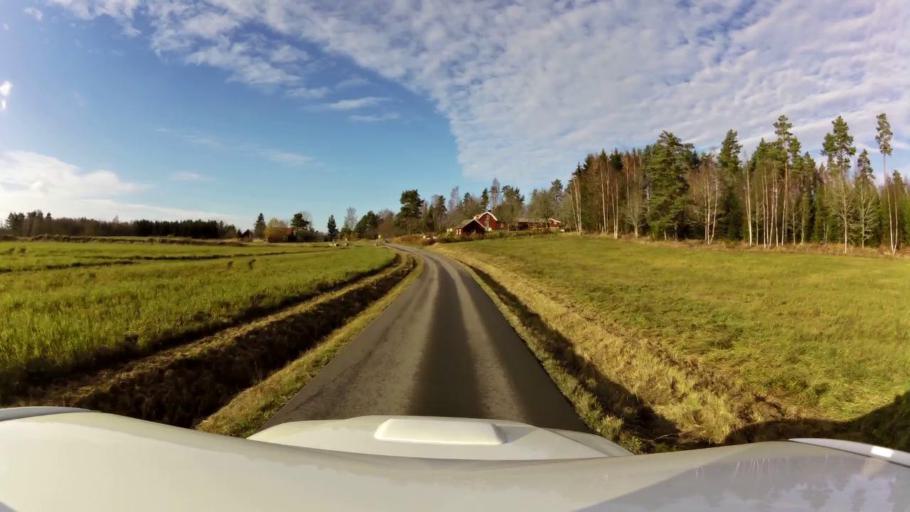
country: SE
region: OEstergoetland
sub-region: Linkopings Kommun
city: Sturefors
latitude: 58.2631
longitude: 15.6827
